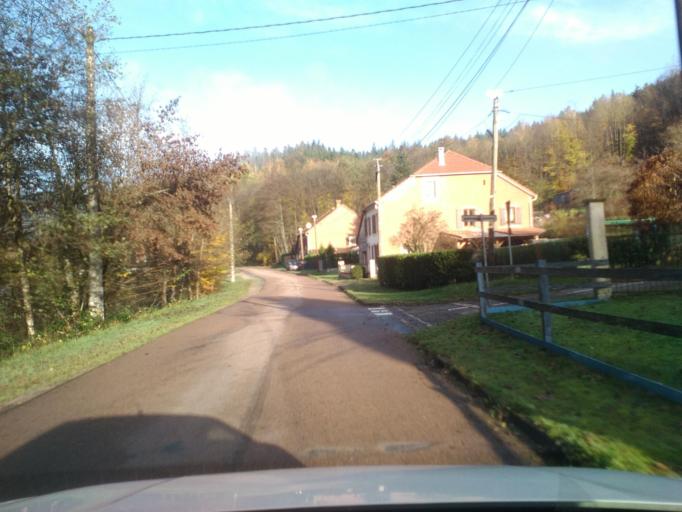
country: FR
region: Lorraine
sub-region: Departement des Vosges
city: Senones
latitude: 48.4239
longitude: 7.0361
